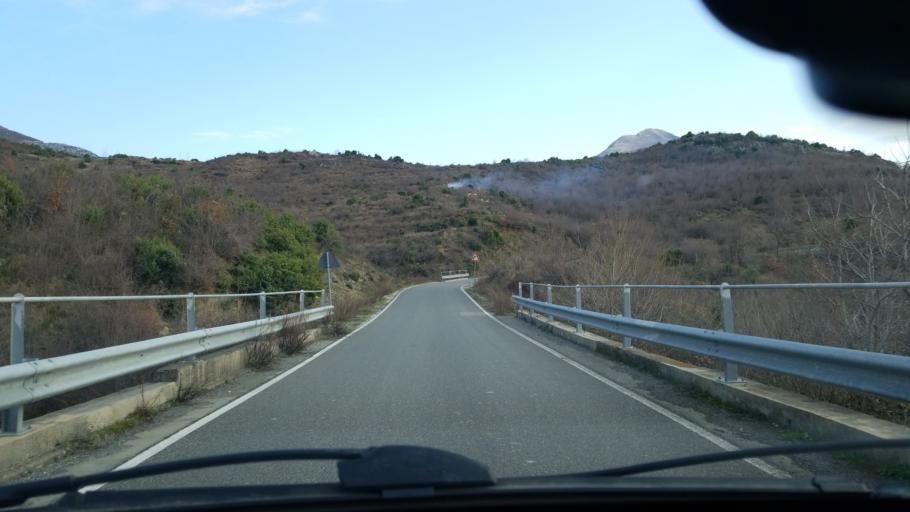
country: AL
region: Lezhe
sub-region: Rrethi i Lezhes
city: Kallmeti i Madh
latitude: 41.8786
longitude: 19.6957
